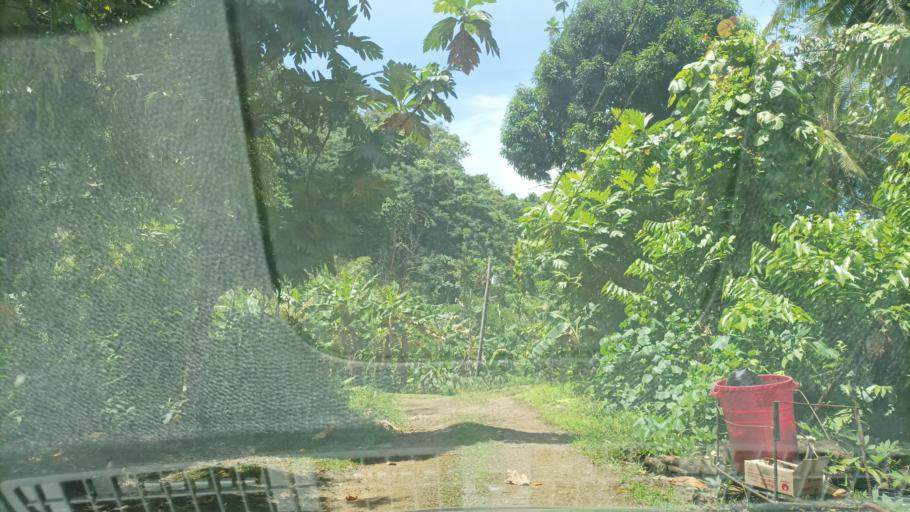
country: FM
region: Kosrae
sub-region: Malem Municipality
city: Malem
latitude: 5.2952
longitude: 163.0232
